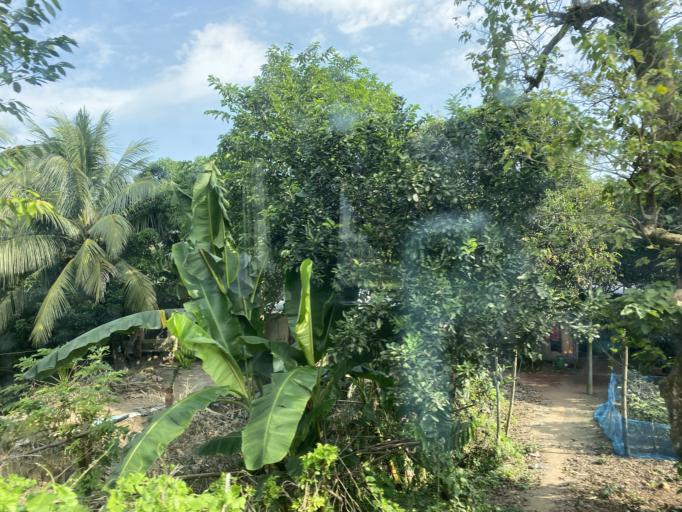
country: BD
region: Dhaka
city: Bhairab Bazar
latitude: 23.9674
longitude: 91.1151
